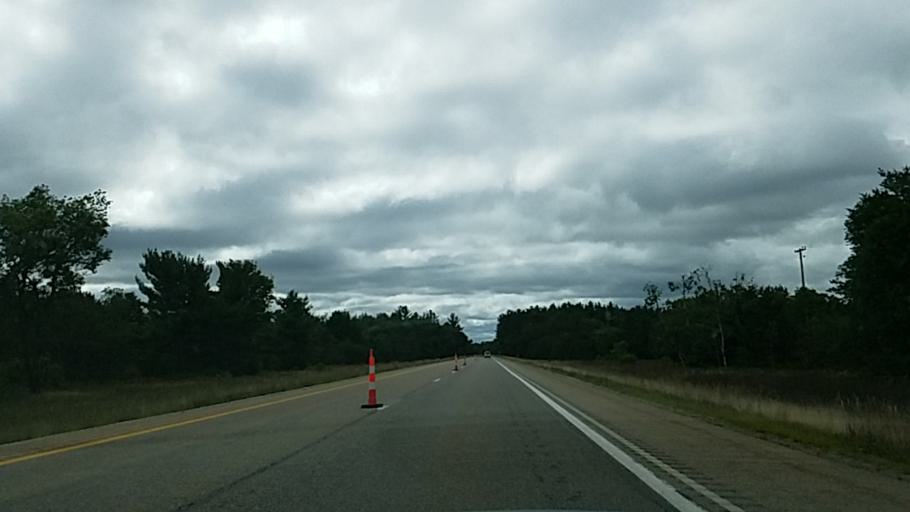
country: US
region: Michigan
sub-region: Crawford County
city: Grayling
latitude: 44.7001
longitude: -84.7001
